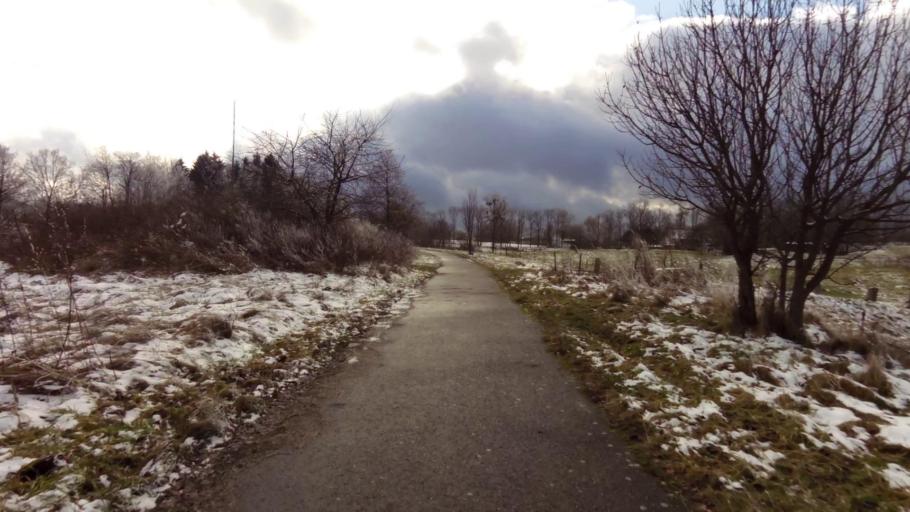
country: PL
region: West Pomeranian Voivodeship
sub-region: Powiat swidwinski
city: Polczyn-Zdroj
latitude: 53.7342
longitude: 16.0431
